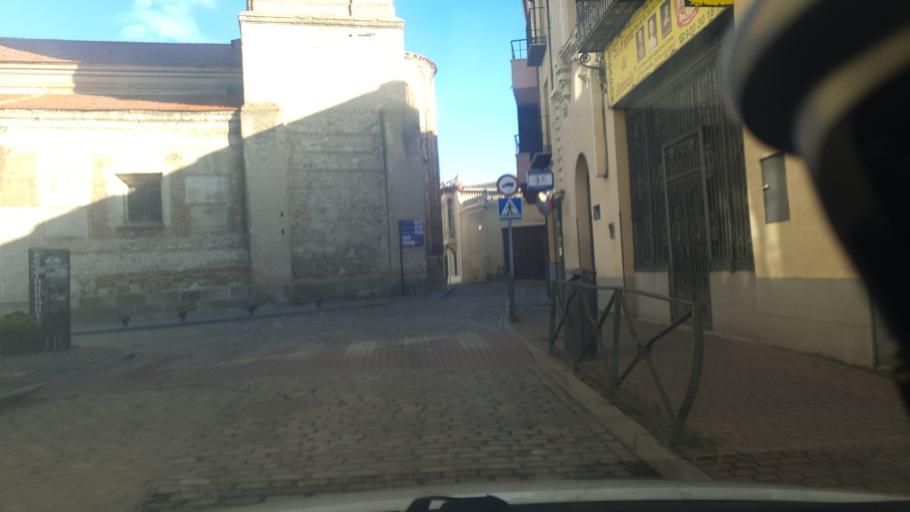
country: ES
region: Castille and Leon
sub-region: Provincia de Avila
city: Arevalo
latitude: 41.0625
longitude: -4.7193
